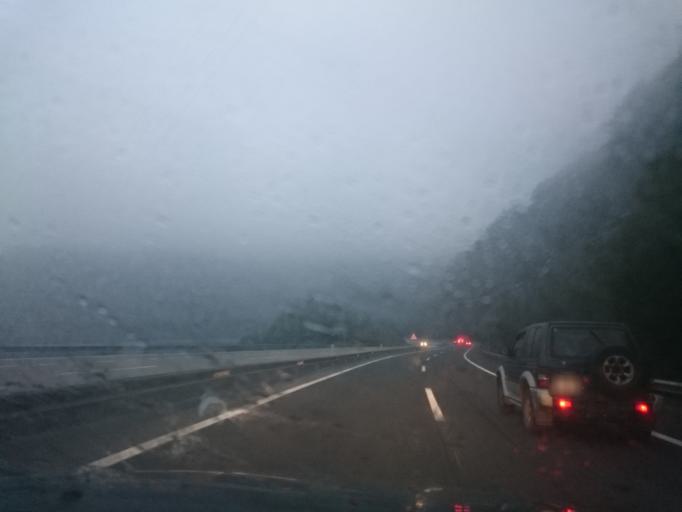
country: ES
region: Asturias
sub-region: Province of Asturias
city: Pola de Lena
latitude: 43.0273
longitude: -5.8229
